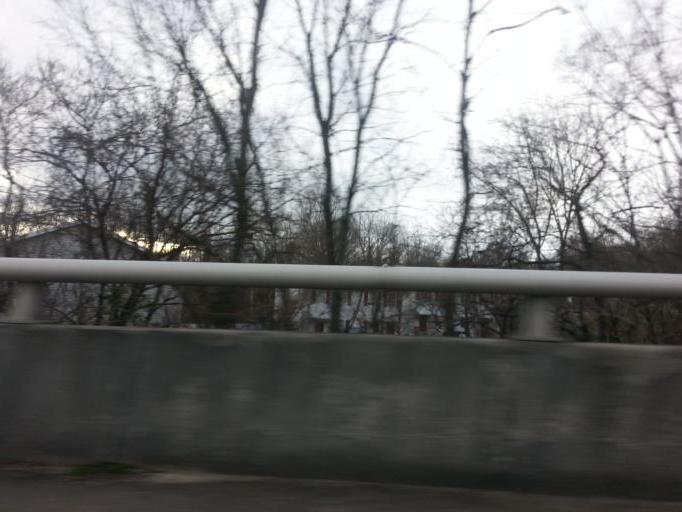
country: US
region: Tennessee
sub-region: Washington County
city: Johnson City
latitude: 36.3133
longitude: -82.3335
